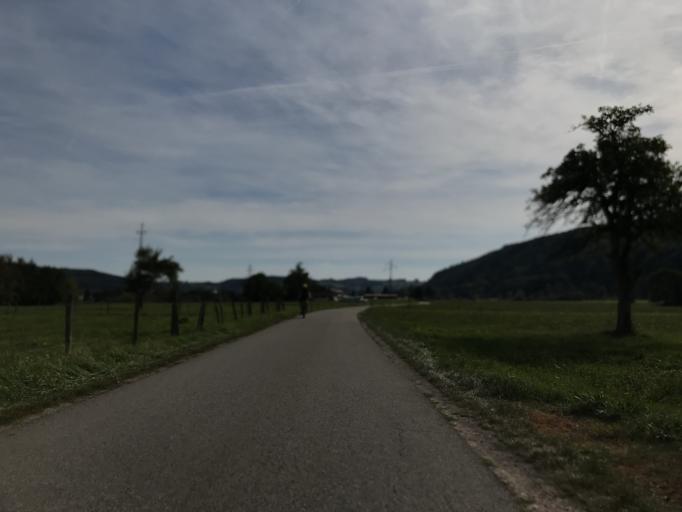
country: DE
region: Baden-Wuerttemberg
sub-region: Freiburg Region
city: Hausen
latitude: 47.6739
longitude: 7.8347
